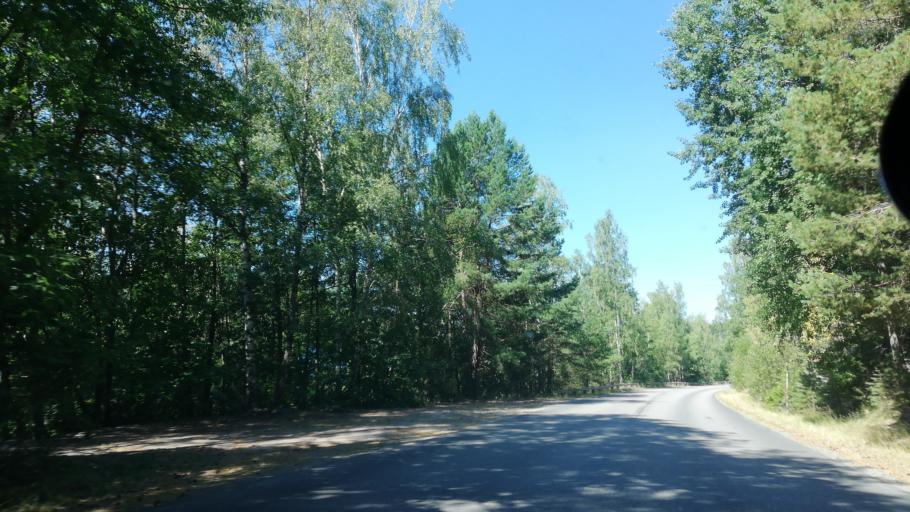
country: SE
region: OEstergoetland
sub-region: Finspangs Kommun
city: Finspang
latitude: 58.7156
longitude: 15.7673
